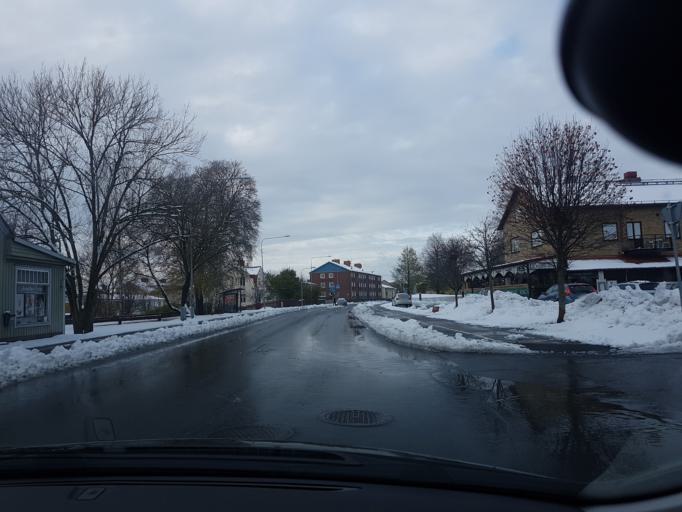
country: SE
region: Joenkoeping
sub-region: Vetlanda Kommun
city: Vetlanda
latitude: 57.4243
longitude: 15.0962
